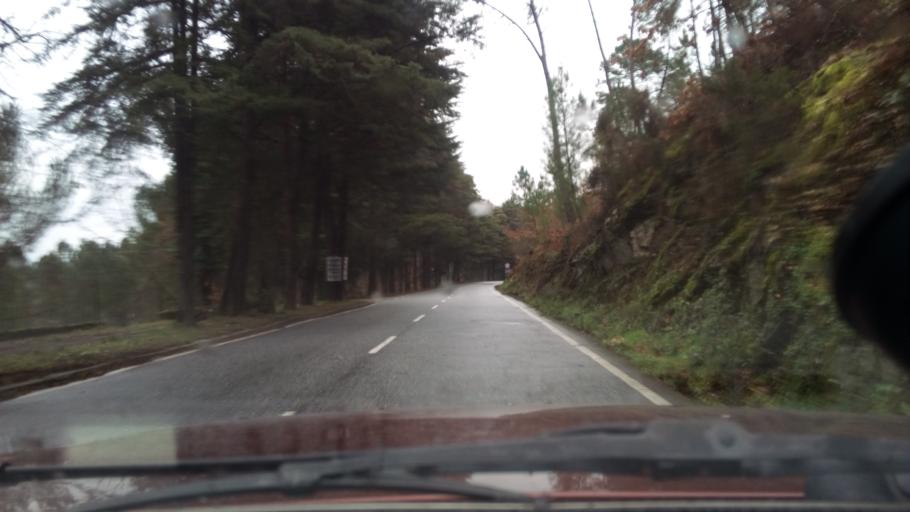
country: PT
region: Viseu
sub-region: Mangualde
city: Mangualde
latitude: 40.6339
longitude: -7.8192
